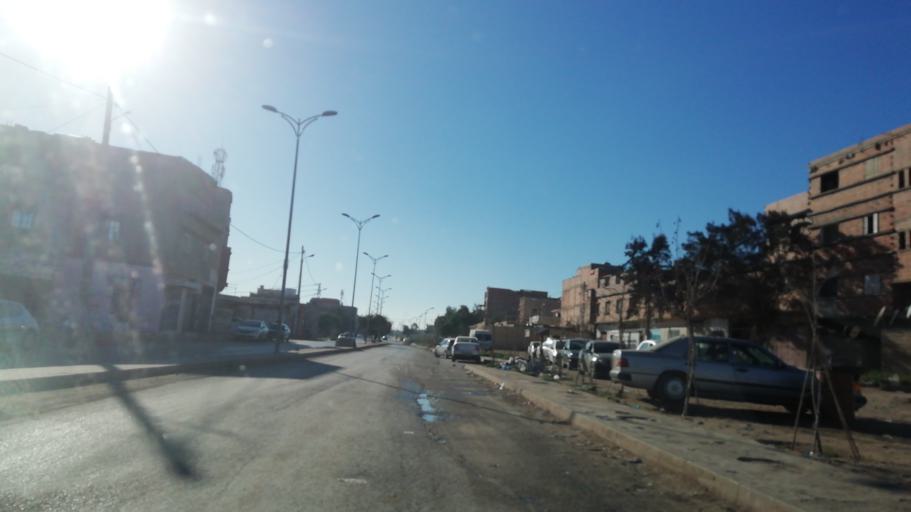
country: DZ
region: Oran
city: Bir el Djir
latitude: 35.7211
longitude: -0.5395
